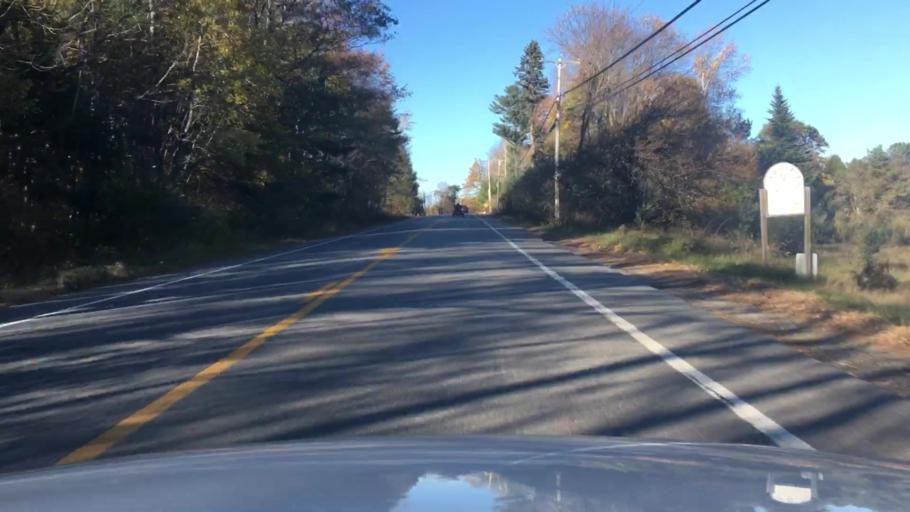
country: US
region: Maine
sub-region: Sagadahoc County
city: Topsham
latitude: 44.0460
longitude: -69.9406
